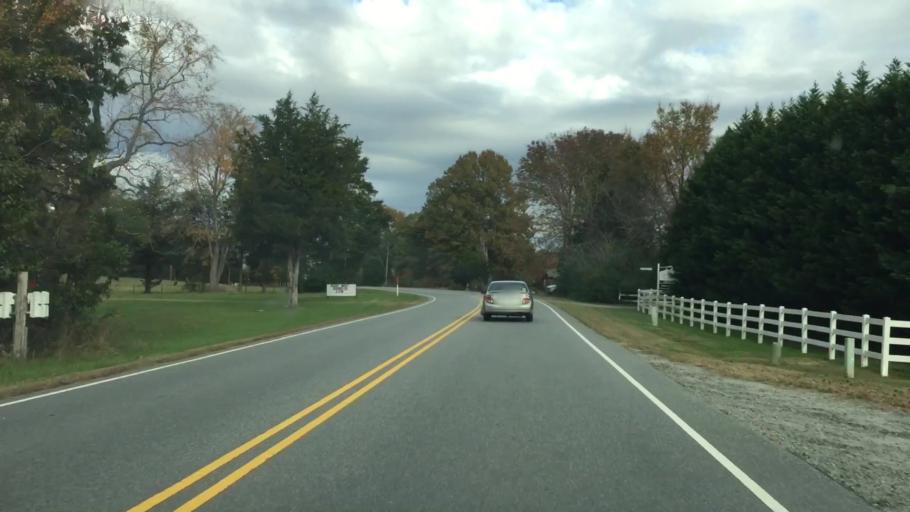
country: US
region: North Carolina
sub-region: Rockingham County
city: Reidsville
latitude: 36.2849
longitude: -79.7530
